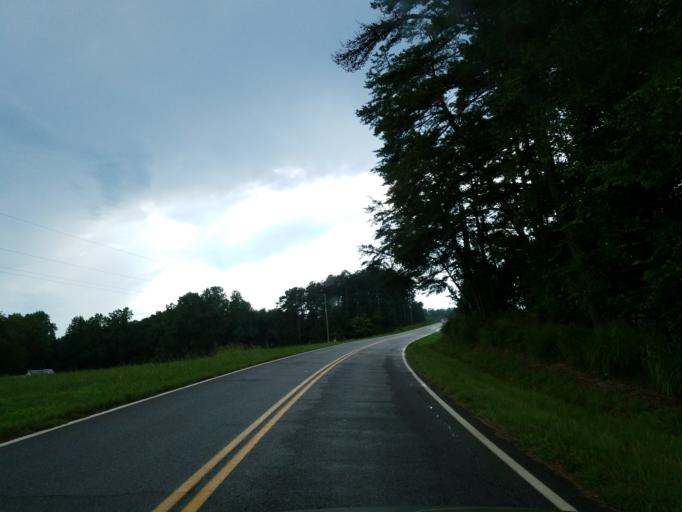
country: US
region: Georgia
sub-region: Lumpkin County
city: Dahlonega
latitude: 34.5596
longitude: -83.8872
